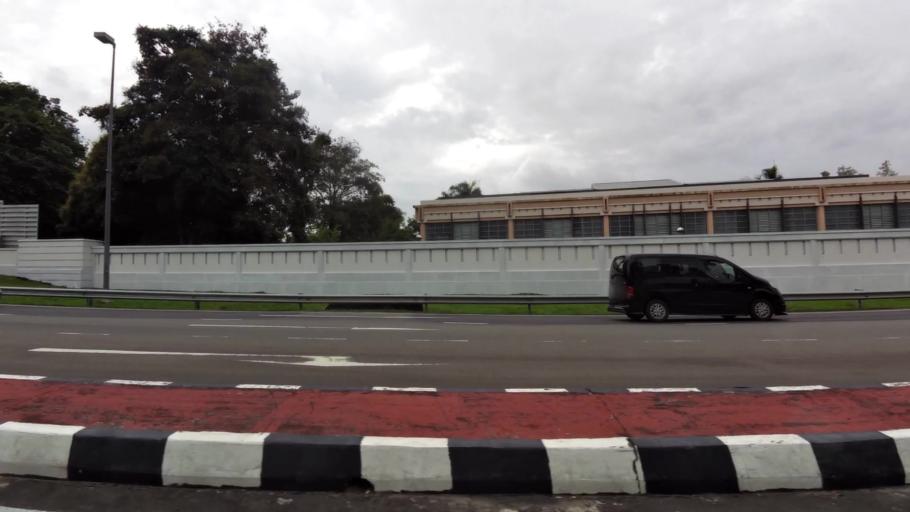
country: BN
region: Brunei and Muara
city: Bandar Seri Begawan
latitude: 4.9150
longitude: 114.9314
